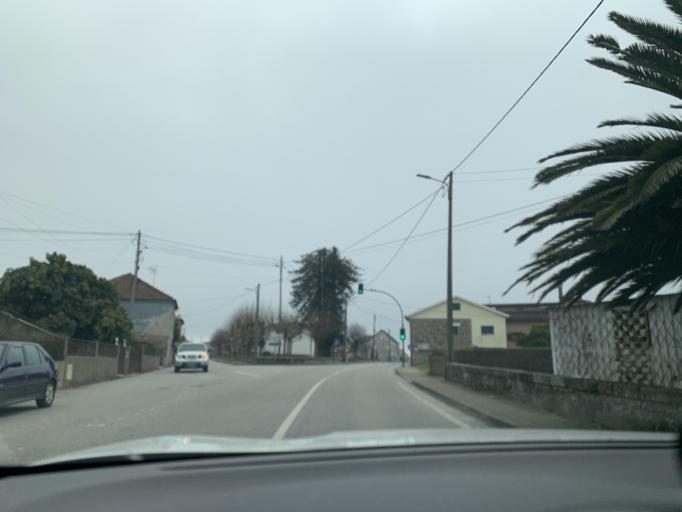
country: PT
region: Viseu
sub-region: Concelho de Tondela
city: Tondela
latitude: 40.4984
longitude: -8.0739
